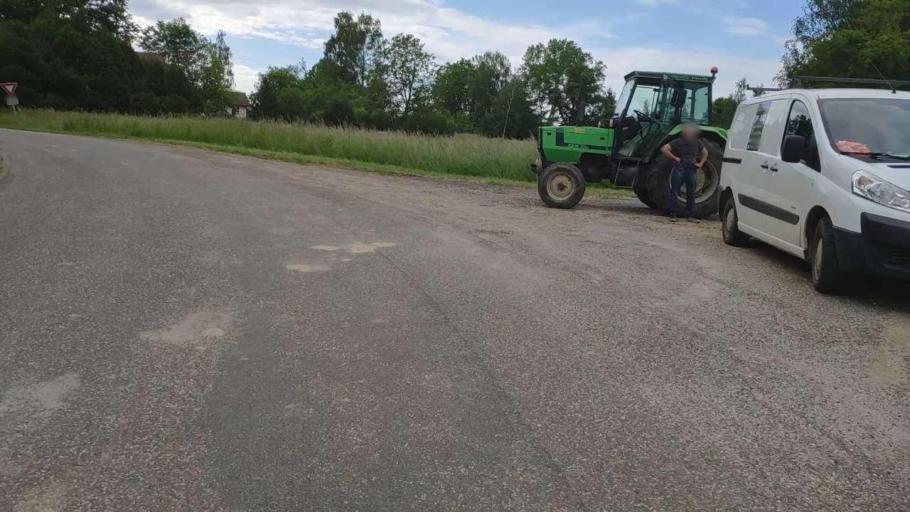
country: FR
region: Franche-Comte
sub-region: Departement du Jura
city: Bletterans
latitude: 46.8084
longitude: 5.5273
